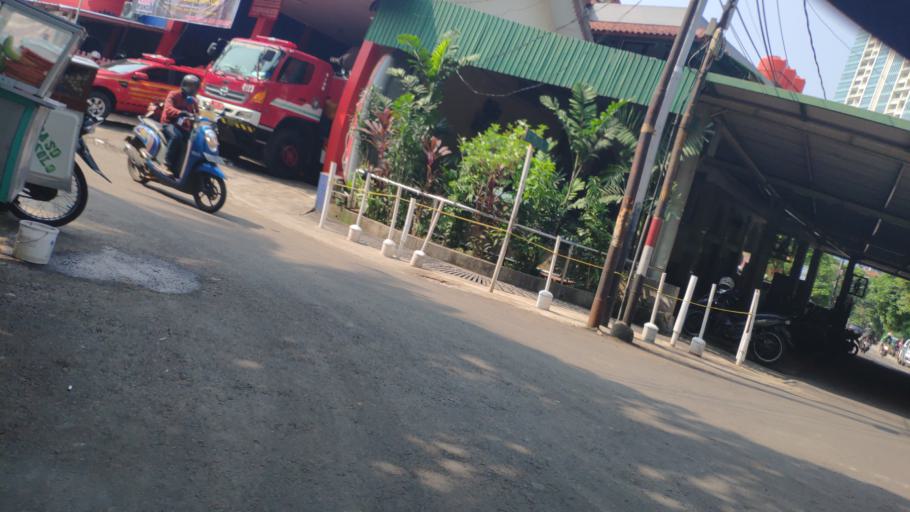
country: ID
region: Jakarta Raya
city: Jakarta
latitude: -6.2492
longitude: 106.7938
